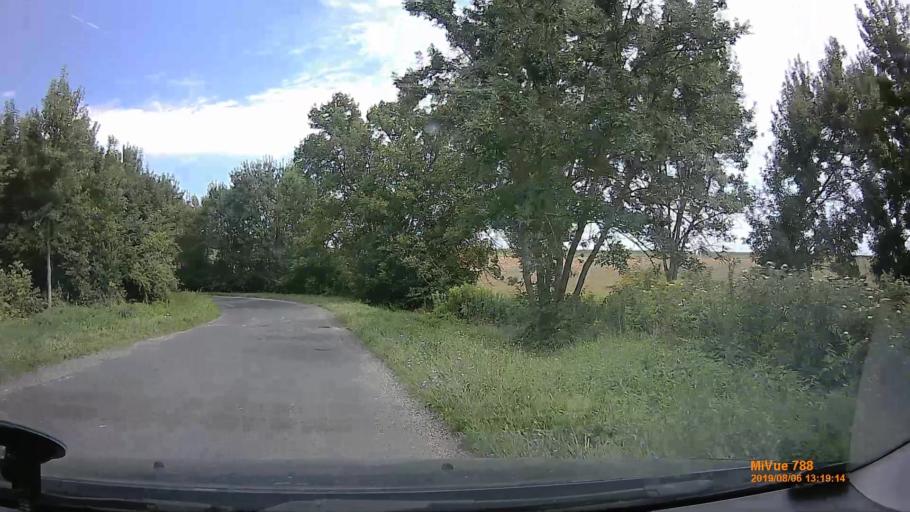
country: HU
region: Zala
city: Pacsa
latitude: 46.6360
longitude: 17.0651
